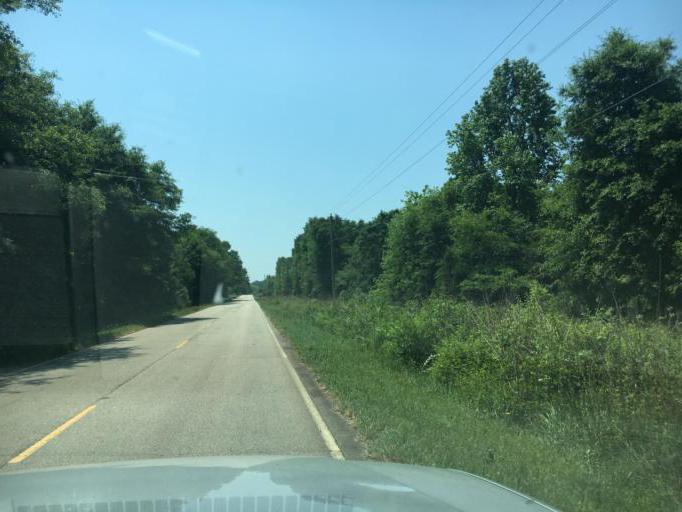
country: US
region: Georgia
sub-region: Hart County
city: Royston
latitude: 34.3543
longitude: -83.0412
